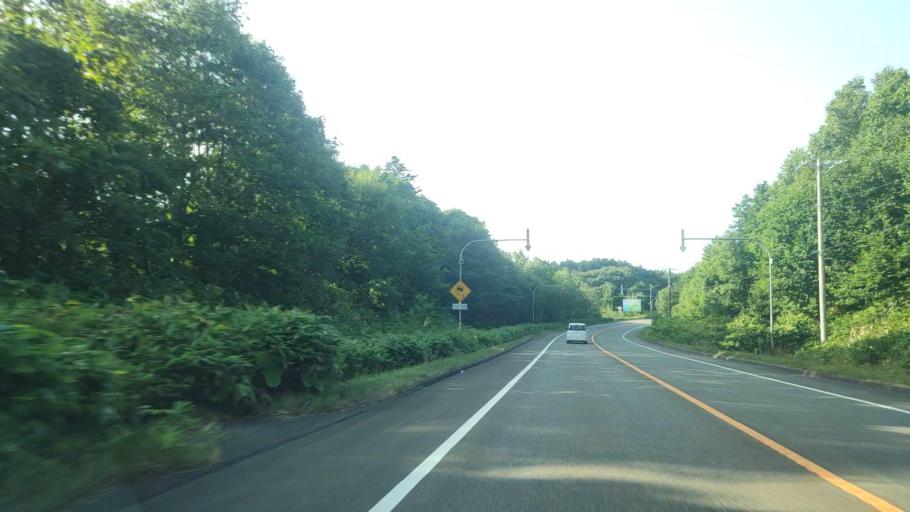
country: JP
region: Hokkaido
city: Makubetsu
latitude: 45.0775
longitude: 141.7536
